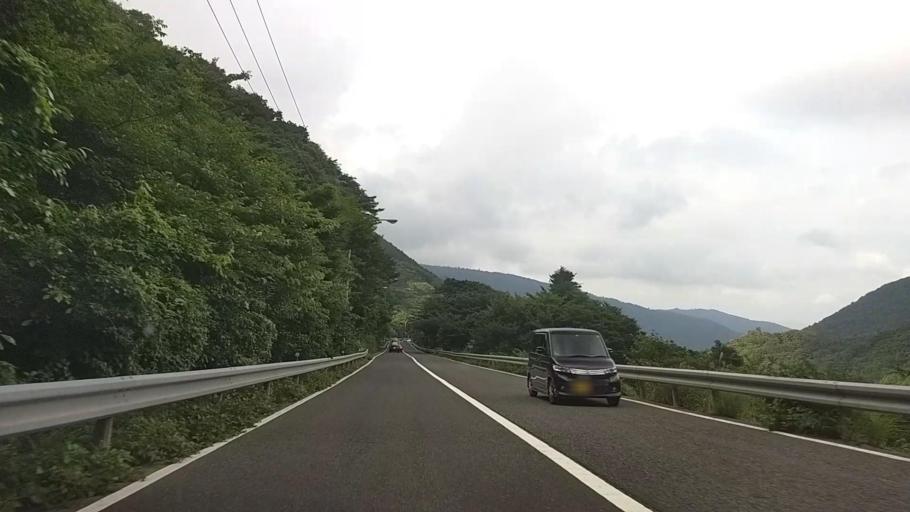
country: JP
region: Kanagawa
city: Hakone
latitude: 35.1999
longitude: 139.0535
